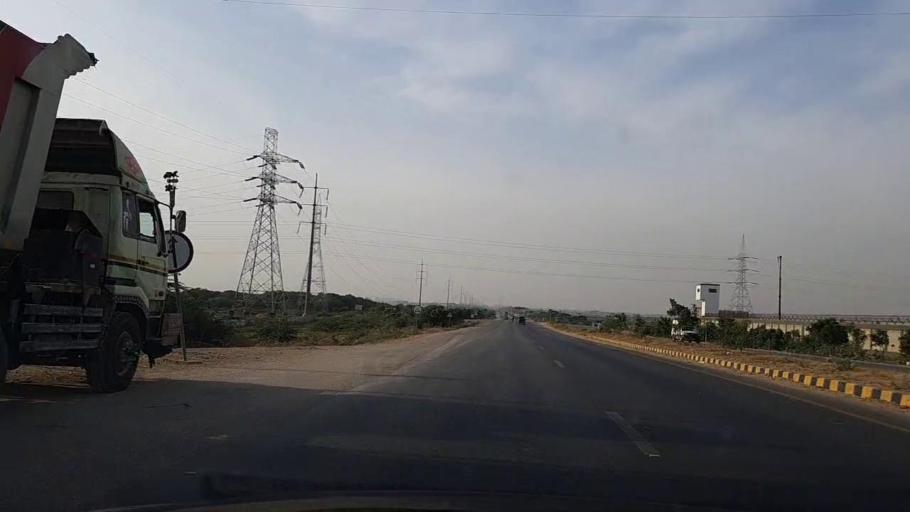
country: PK
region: Sindh
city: Gharo
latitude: 24.7670
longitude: 67.5509
